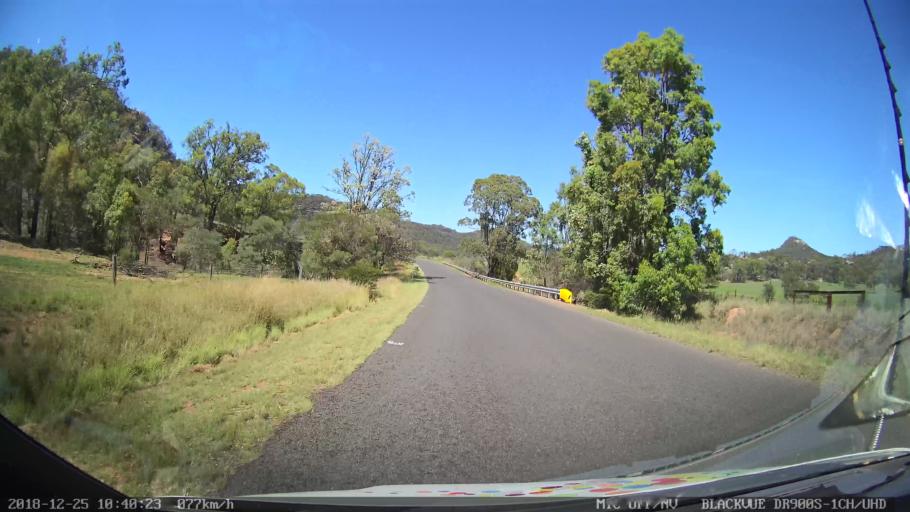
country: AU
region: New South Wales
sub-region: Upper Hunter Shire
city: Merriwa
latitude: -32.4071
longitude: 150.3437
